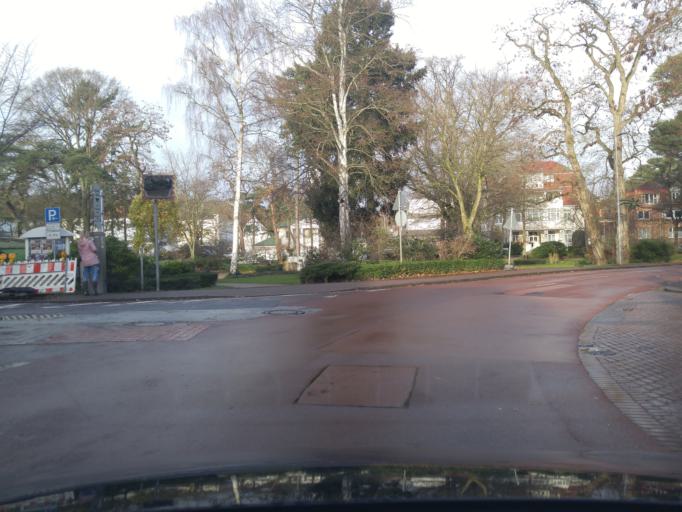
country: DE
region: Schleswig-Holstein
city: Timmendorfer Strand
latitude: 53.9996
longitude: 10.7788
